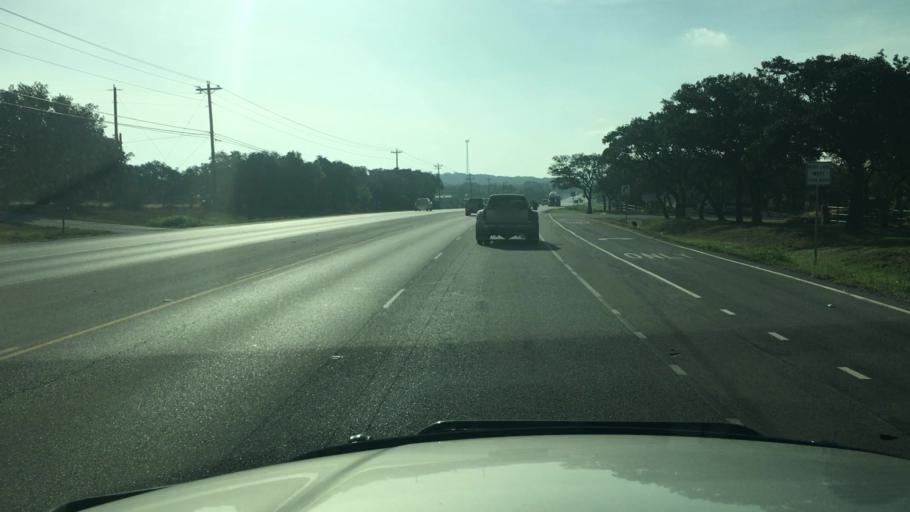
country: US
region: Texas
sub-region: Hays County
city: Dripping Springs
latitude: 30.2058
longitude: -98.1279
